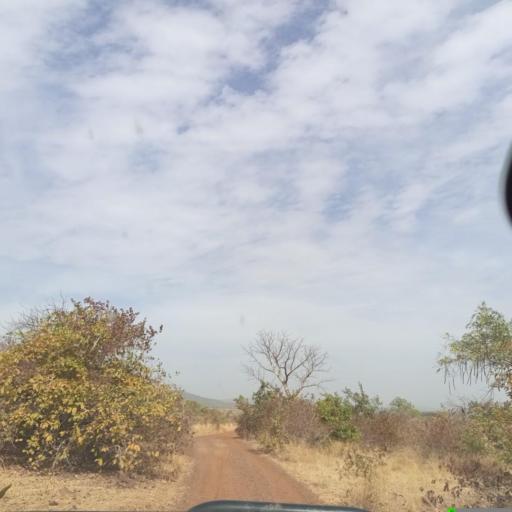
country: ML
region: Koulikoro
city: Koulikoro
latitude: 13.1616
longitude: -7.7271
